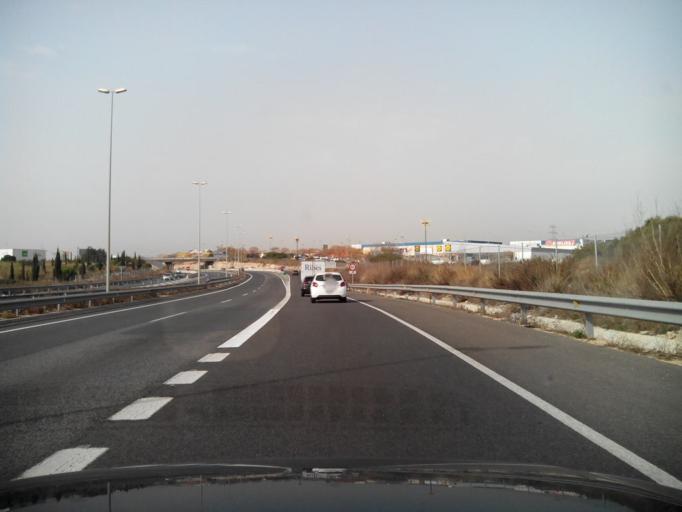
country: ES
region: Catalonia
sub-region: Provincia de Tarragona
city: Constanti
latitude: 41.1319
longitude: 1.2105
